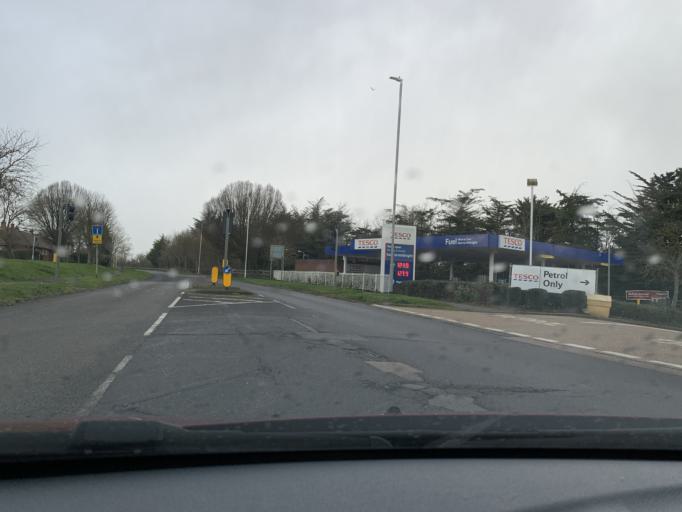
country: GB
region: England
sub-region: Kent
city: Hawkinge
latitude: 51.0902
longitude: 1.1288
